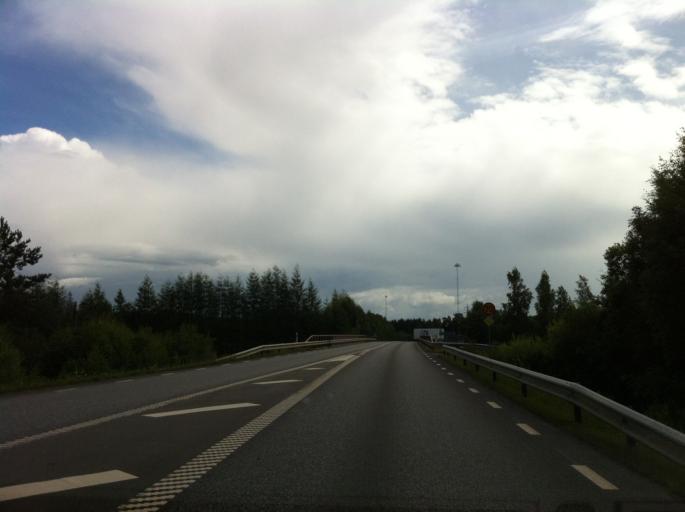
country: SE
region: Skane
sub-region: Hassleholms Kommun
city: Bjarnum
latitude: 56.2023
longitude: 13.6598
